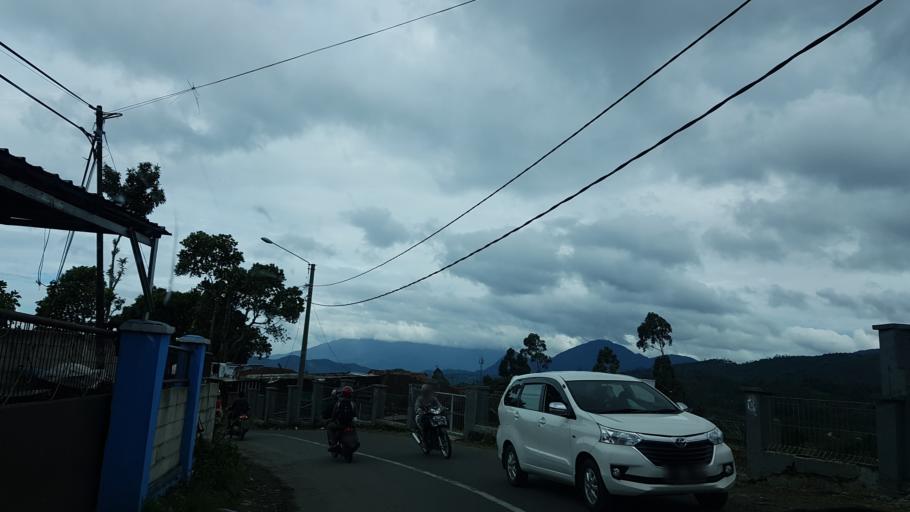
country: ID
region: West Java
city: Banjar
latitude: -7.1222
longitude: 107.4284
